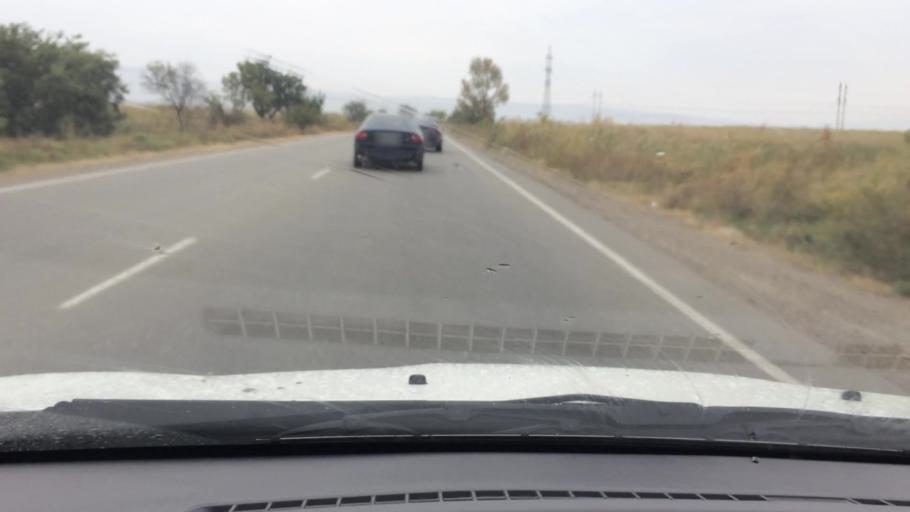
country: GE
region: Kvemo Kartli
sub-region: Marneuli
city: Marneuli
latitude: 41.5382
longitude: 44.7769
